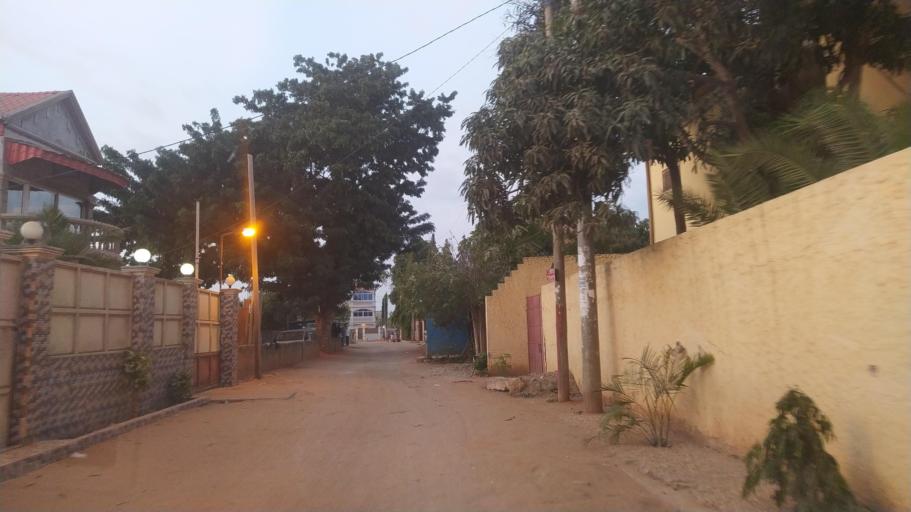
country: AO
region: Luanda
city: Luanda
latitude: -8.8967
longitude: 13.2047
